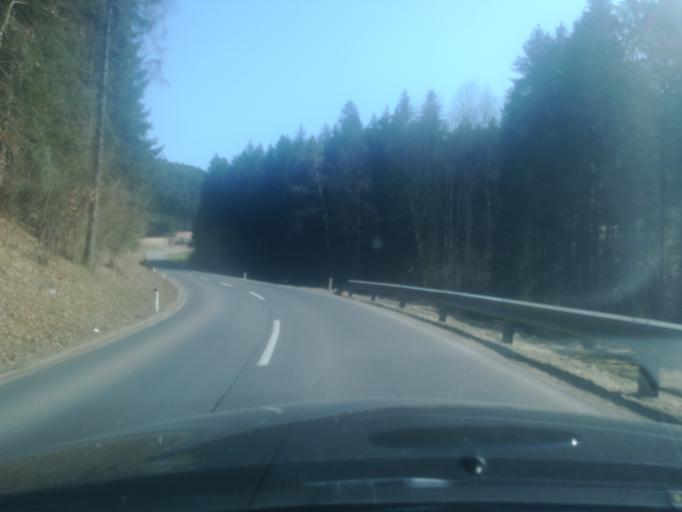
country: AT
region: Upper Austria
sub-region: Politischer Bezirk Freistadt
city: Freistadt
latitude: 48.4376
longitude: 14.5581
